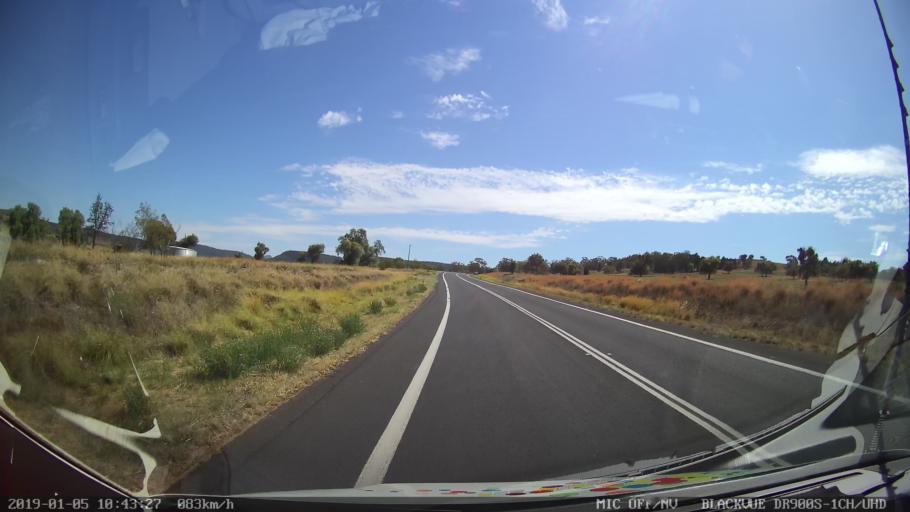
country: AU
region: New South Wales
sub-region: Warrumbungle Shire
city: Coonabarabran
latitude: -31.4646
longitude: 148.9881
